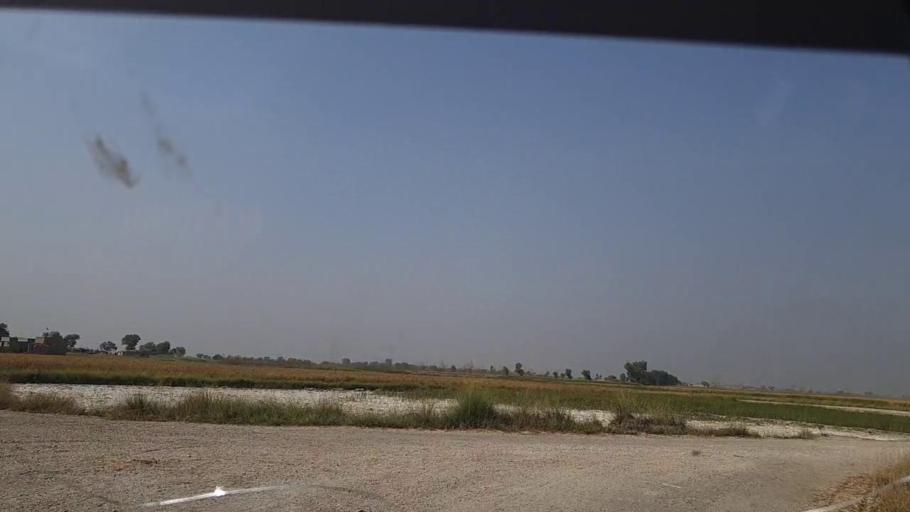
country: PK
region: Sindh
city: Shikarpur
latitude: 28.0915
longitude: 68.5994
